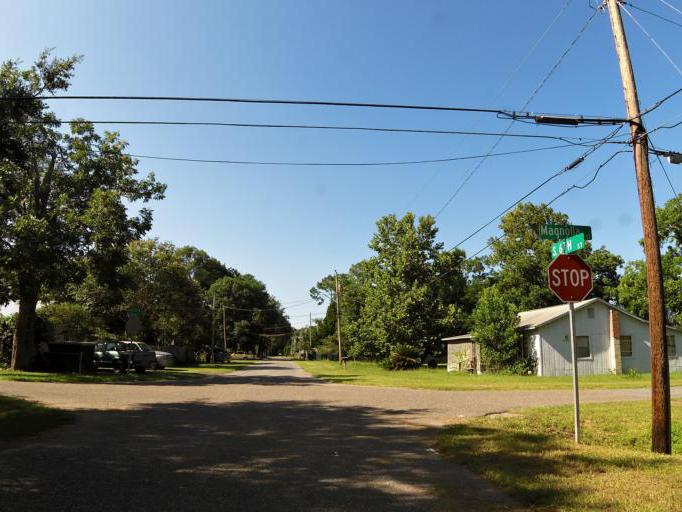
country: US
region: Florida
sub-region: Nassau County
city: Fernandina Beach
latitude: 30.6544
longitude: -81.4629
